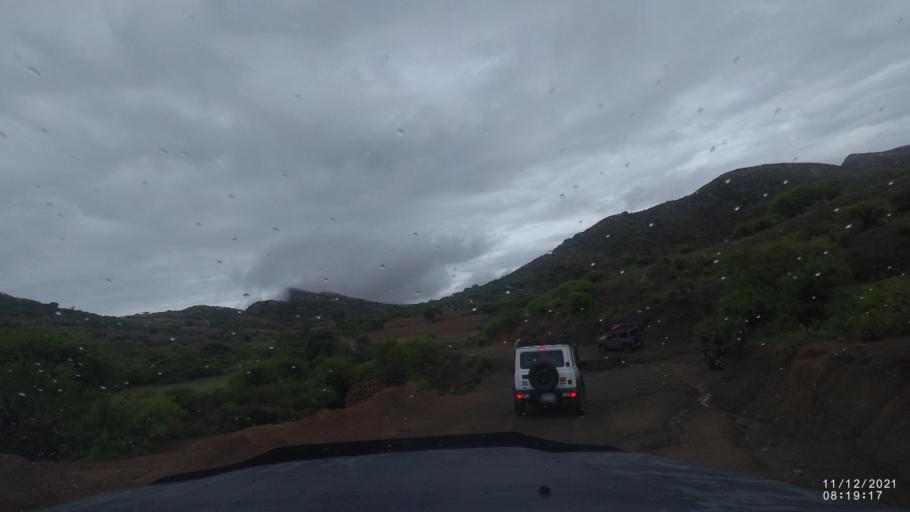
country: BO
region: Cochabamba
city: Tarata
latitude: -17.9401
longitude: -65.9303
